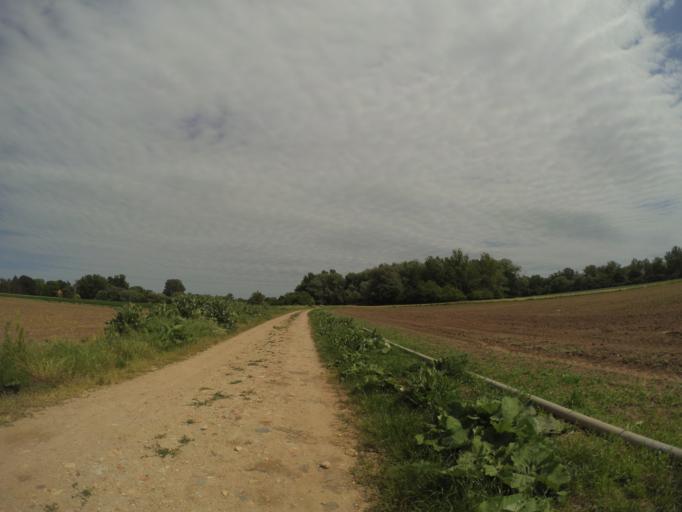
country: CZ
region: Central Bohemia
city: Milovice
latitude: 50.1765
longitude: 14.8906
